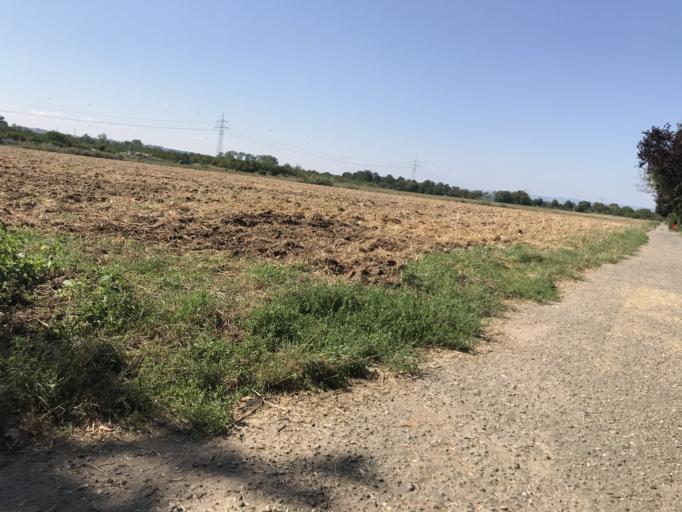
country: DE
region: Hesse
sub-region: Regierungsbezirk Darmstadt
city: Ginsheim-Gustavsburg
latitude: 49.9806
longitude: 8.3559
